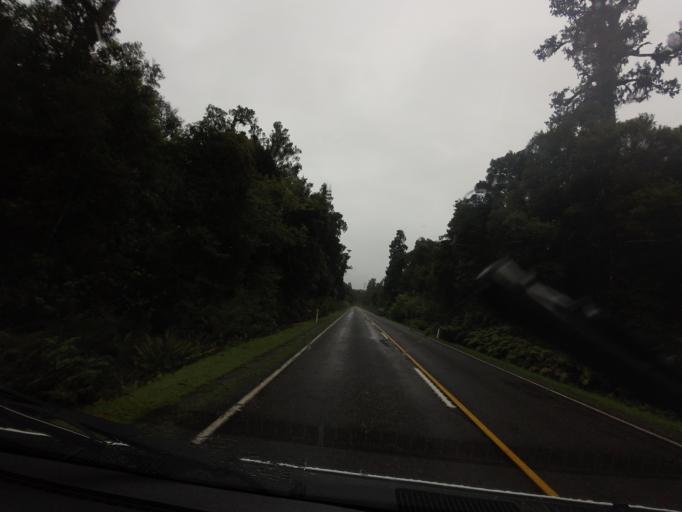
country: NZ
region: Otago
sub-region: Queenstown-Lakes District
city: Wanaka
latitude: -43.8474
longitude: 169.0588
